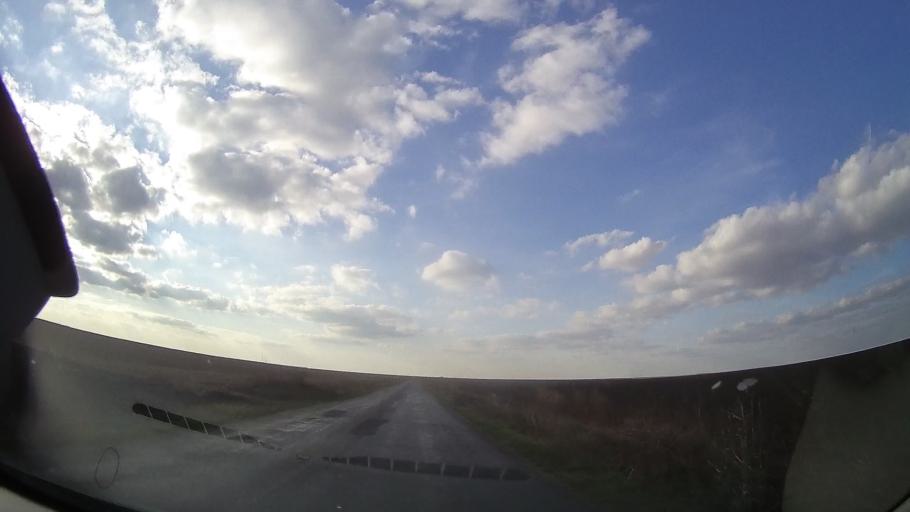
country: RO
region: Constanta
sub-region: Comuna Negru Voda
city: Negru Voda
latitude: 43.8205
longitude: 28.1715
